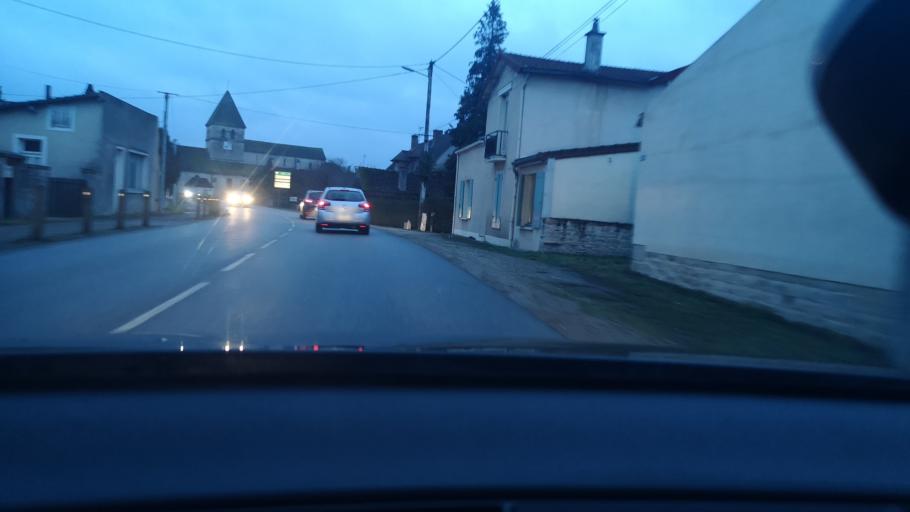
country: FR
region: Bourgogne
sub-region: Departement de Saone-et-Loire
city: Demigny
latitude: 46.9490
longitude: 4.9087
